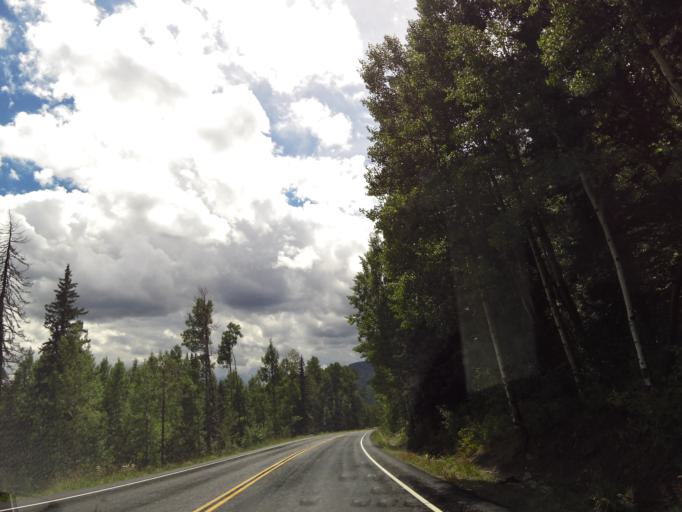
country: US
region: Colorado
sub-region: San Juan County
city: Silverton
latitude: 37.6681
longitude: -107.7961
